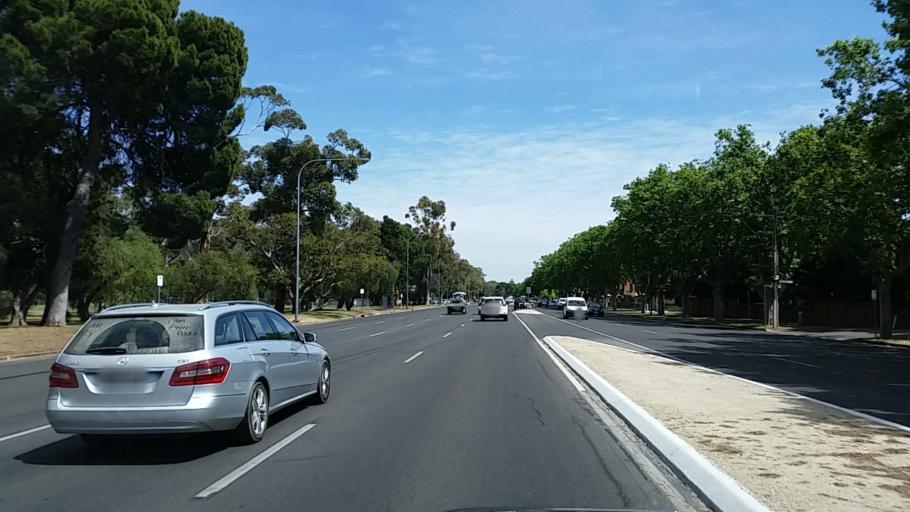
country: AU
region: South Australia
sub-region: Adelaide
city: Adelaide
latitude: -34.9266
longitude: 138.6214
